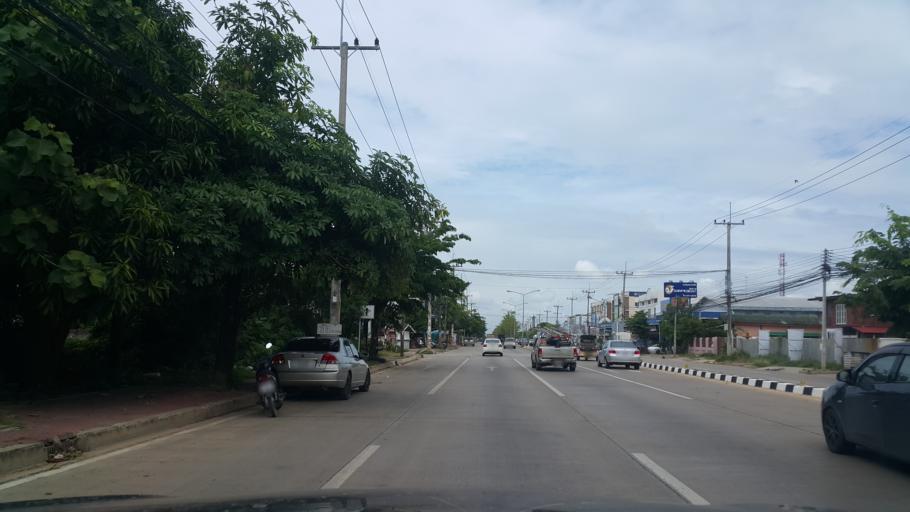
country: TH
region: Phitsanulok
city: Phitsanulok
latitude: 16.8186
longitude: 100.2423
